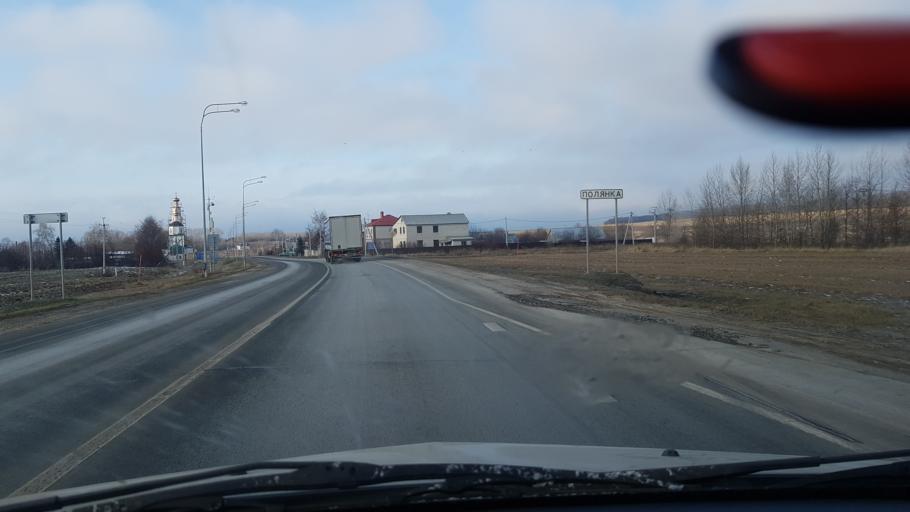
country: RU
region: Tatarstan
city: Laishevo
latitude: 55.3917
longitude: 49.8062
